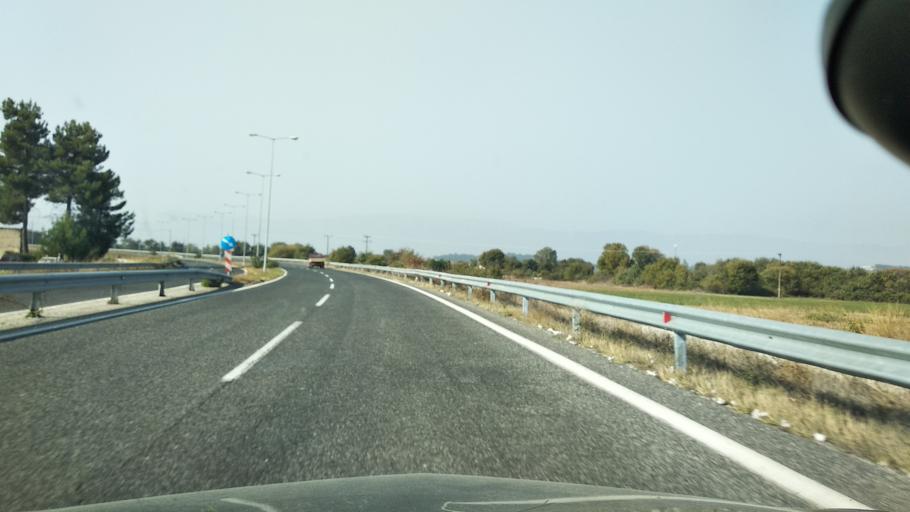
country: GR
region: Thessaly
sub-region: Trikala
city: Megalochori
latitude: 39.5662
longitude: 21.8068
